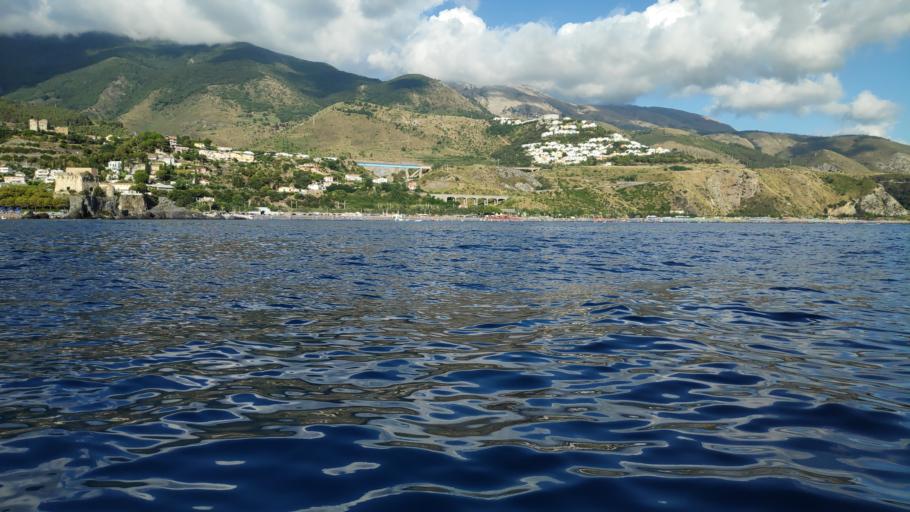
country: IT
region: Calabria
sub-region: Provincia di Cosenza
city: Praia a Mare
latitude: 39.8706
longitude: 15.7814
